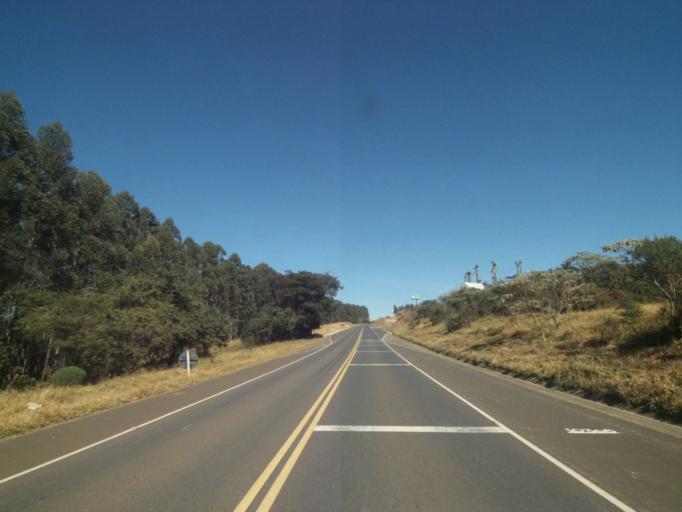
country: BR
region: Parana
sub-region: Tibagi
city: Tibagi
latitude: -24.5195
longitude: -50.4372
